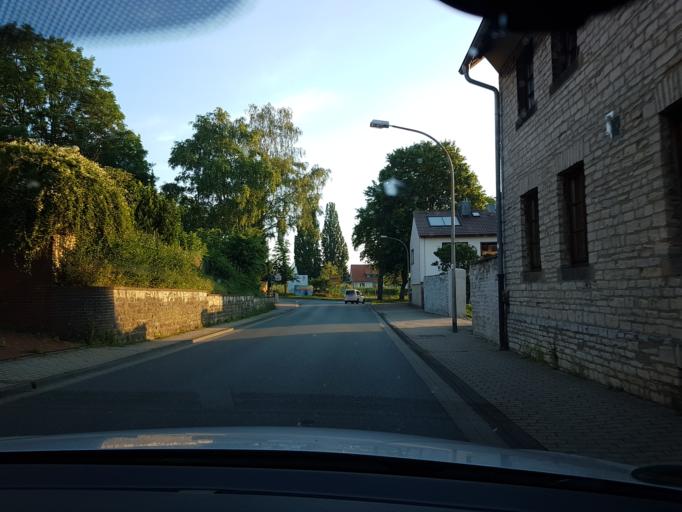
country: DE
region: Lower Saxony
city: Schoningen
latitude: 52.1403
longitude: 10.9600
